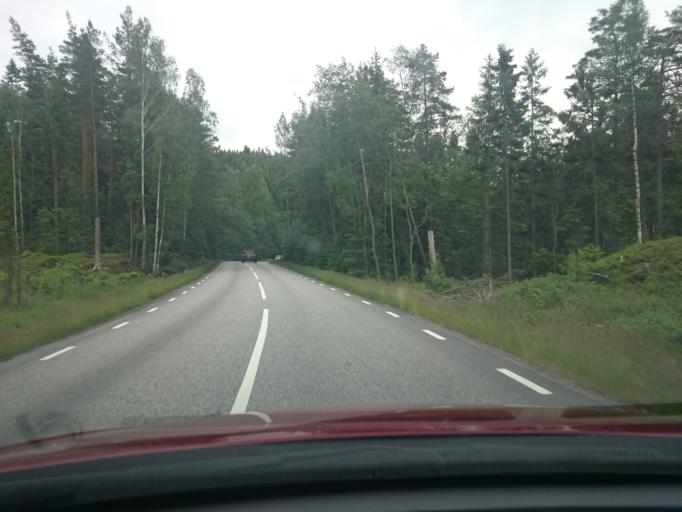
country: SE
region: Vaestra Goetaland
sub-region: Lerums Kommun
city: Stenkullen
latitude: 57.7496
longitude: 12.3287
